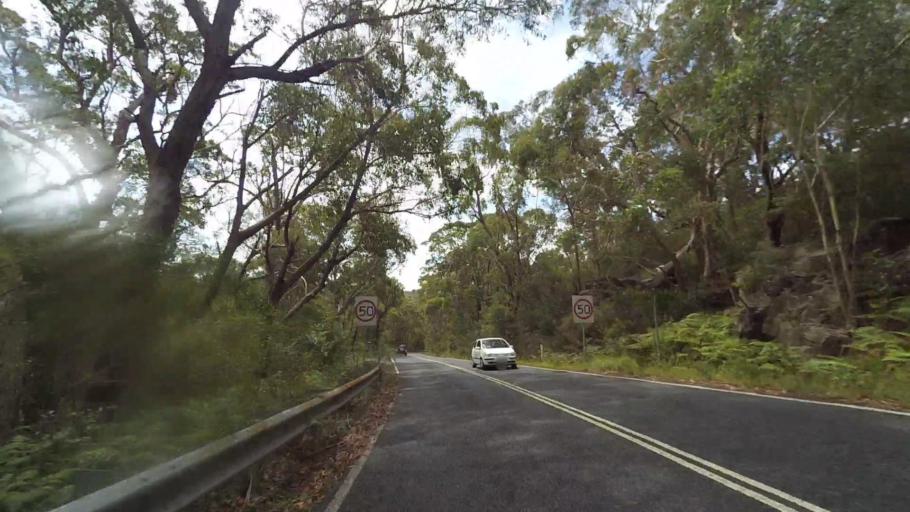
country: AU
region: New South Wales
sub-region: Sutherland Shire
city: Loftus
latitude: -34.0775
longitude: 151.0571
